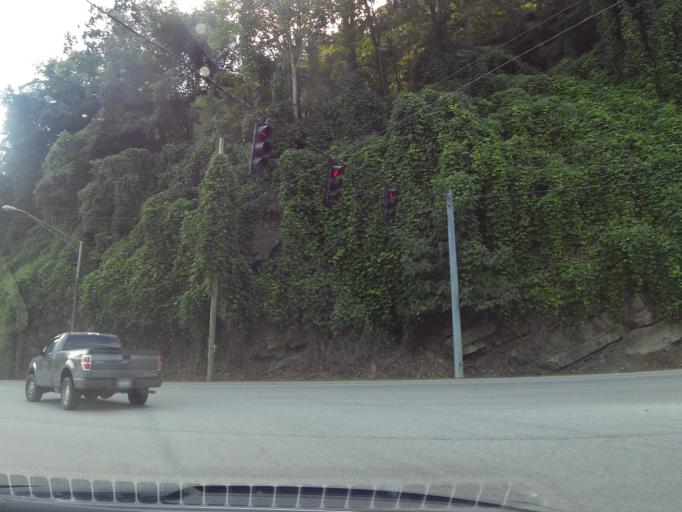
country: US
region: Kentucky
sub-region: Bell County
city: Pineville
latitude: 36.7477
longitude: -83.6934
